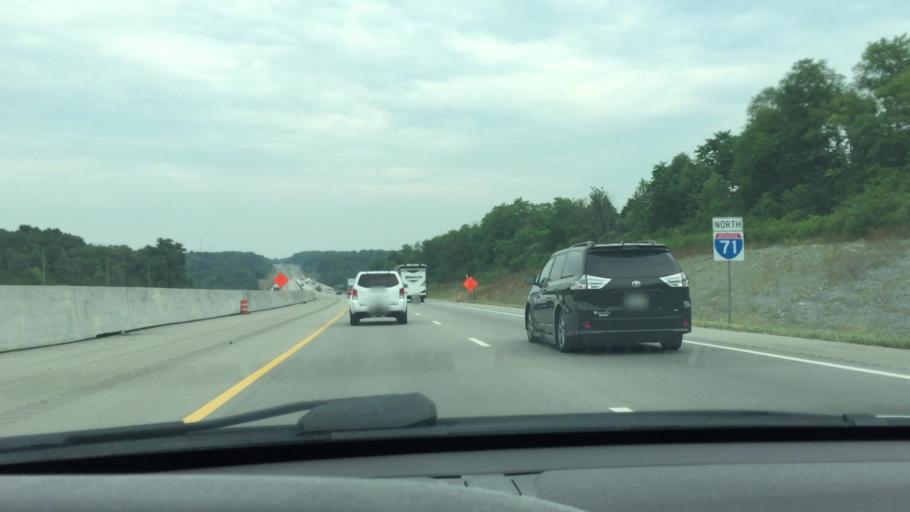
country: US
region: Ohio
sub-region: Warren County
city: Morrow
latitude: 39.4164
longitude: -84.1130
